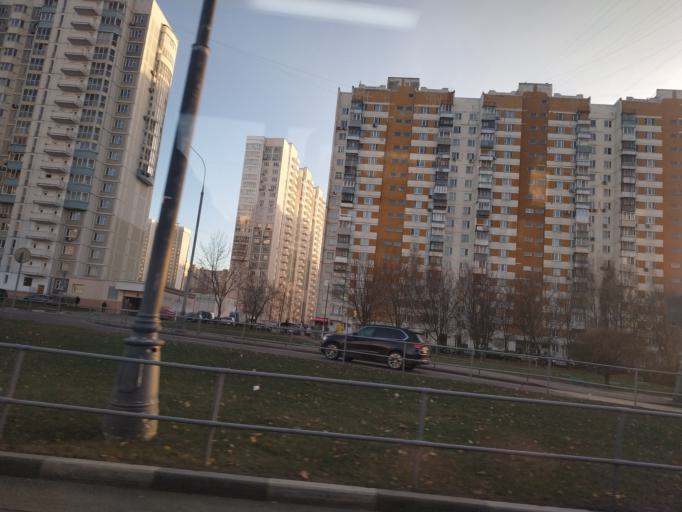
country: RU
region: Moscow
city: Chertanovo Yuzhnoye
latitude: 55.5957
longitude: 37.5960
